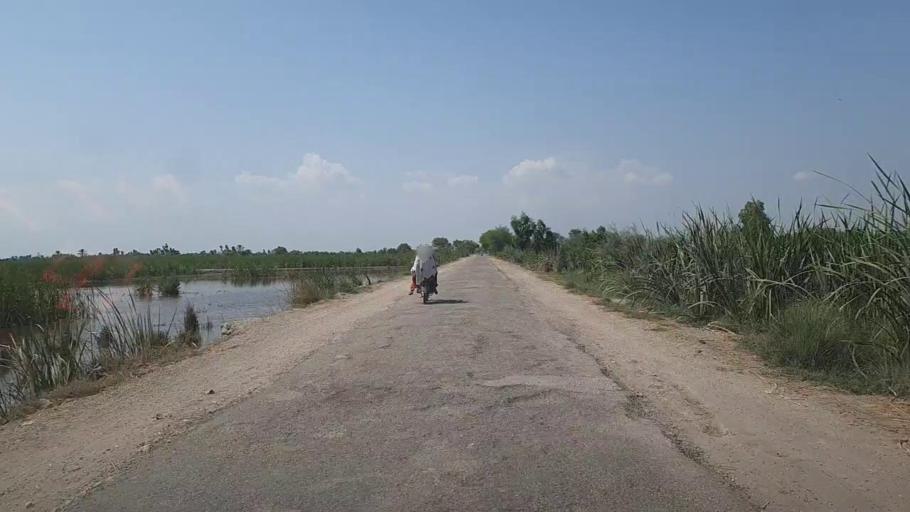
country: PK
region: Sindh
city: Khairpur
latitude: 28.0720
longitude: 69.6409
